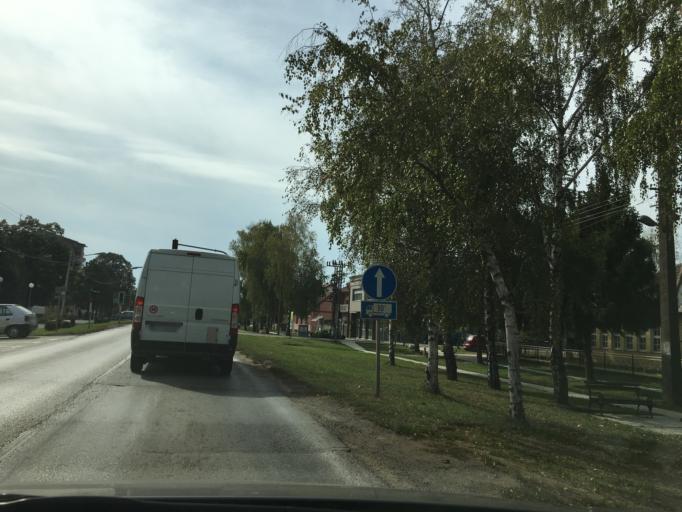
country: RS
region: Autonomna Pokrajina Vojvodina
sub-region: Juznobacki Okrug
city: Temerin
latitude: 45.3918
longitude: 19.8810
